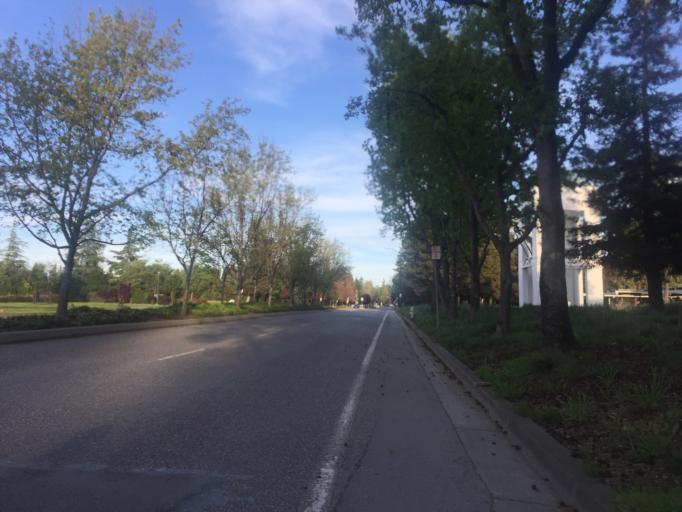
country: US
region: California
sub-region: Santa Clara County
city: Mountain View
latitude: 37.4207
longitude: -122.0824
